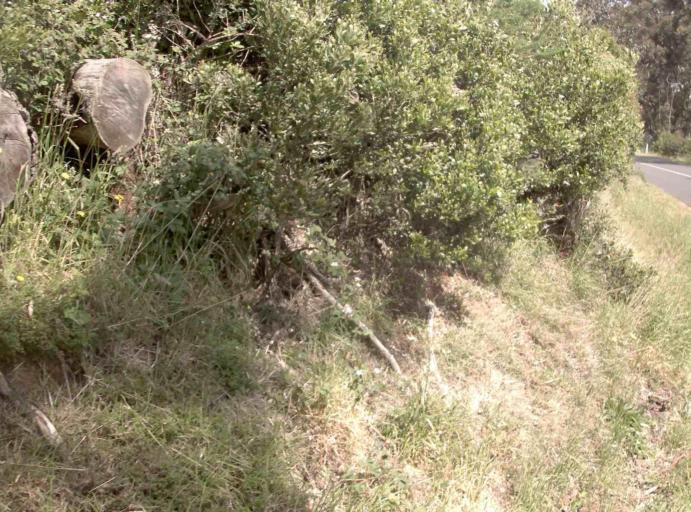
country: AU
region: Victoria
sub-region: Latrobe
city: Traralgon
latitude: -38.3517
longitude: 146.5679
